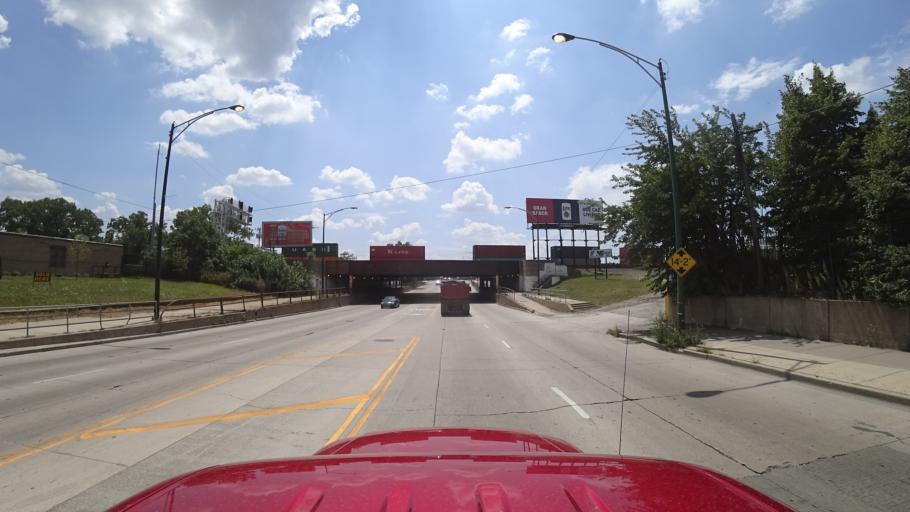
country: US
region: Illinois
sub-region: Cook County
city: Chicago
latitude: 41.8209
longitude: -87.6653
